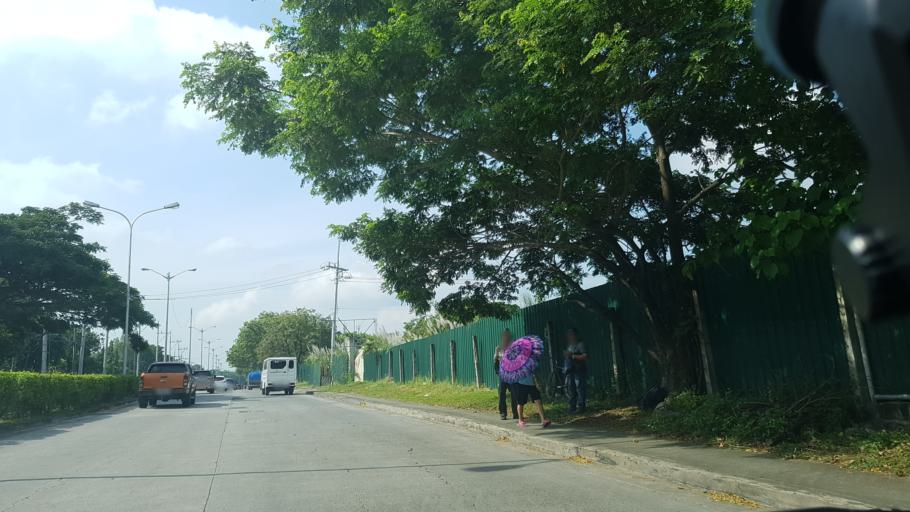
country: PH
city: Sambayanihan People's Village
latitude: 14.4029
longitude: 121.0120
